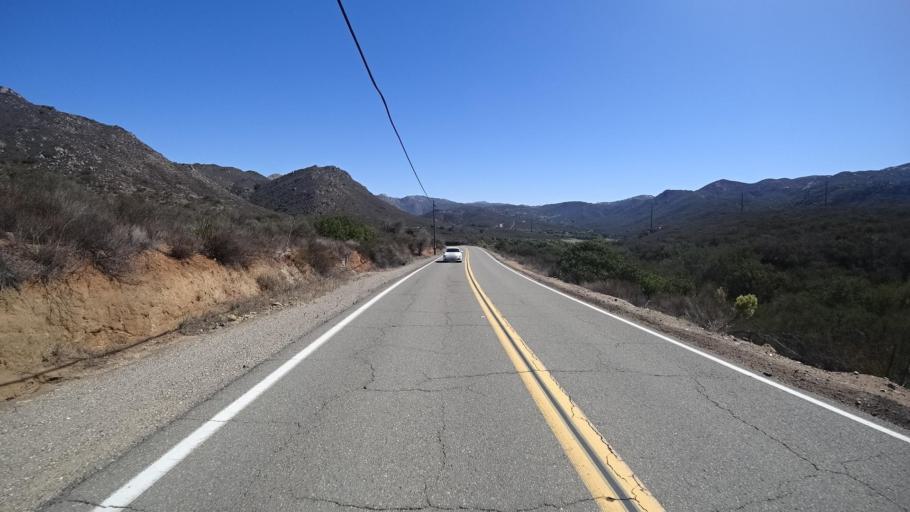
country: US
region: California
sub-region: San Diego County
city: Alpine
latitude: 32.7994
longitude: -116.7565
